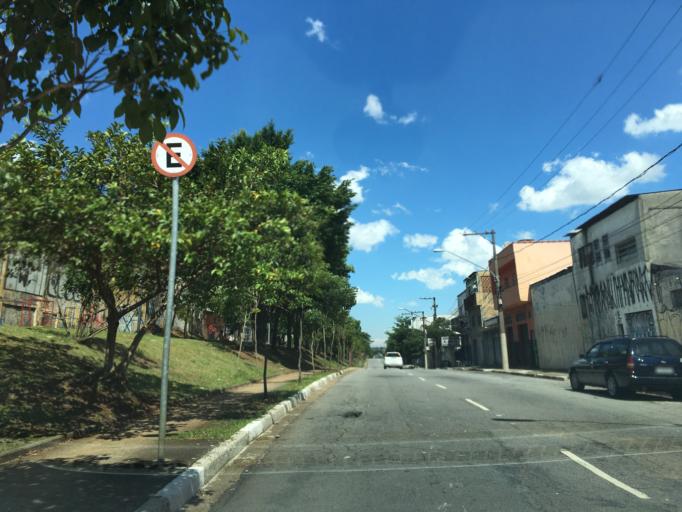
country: BR
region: Sao Paulo
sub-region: Sao Caetano Do Sul
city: Sao Caetano do Sul
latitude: -23.5743
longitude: -46.5615
